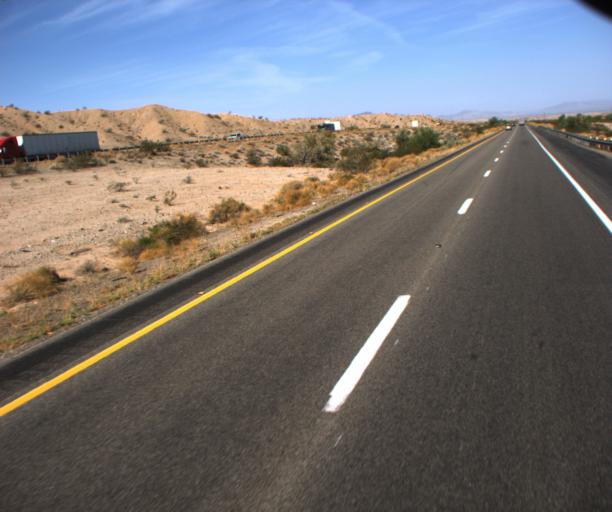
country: US
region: Arizona
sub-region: Mohave County
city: Desert Hills
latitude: 34.7285
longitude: -114.3563
